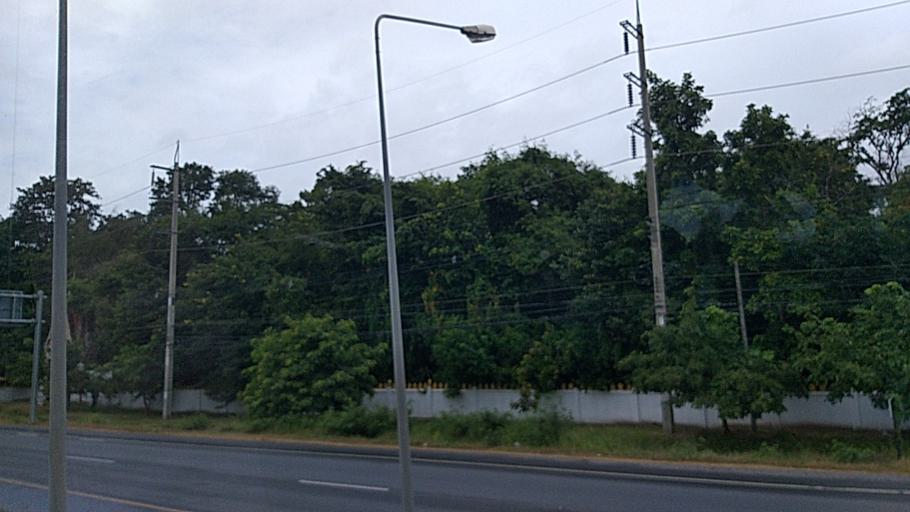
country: TH
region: Maha Sarakham
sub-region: Amphoe Borabue
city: Borabue
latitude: 16.0472
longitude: 103.1257
